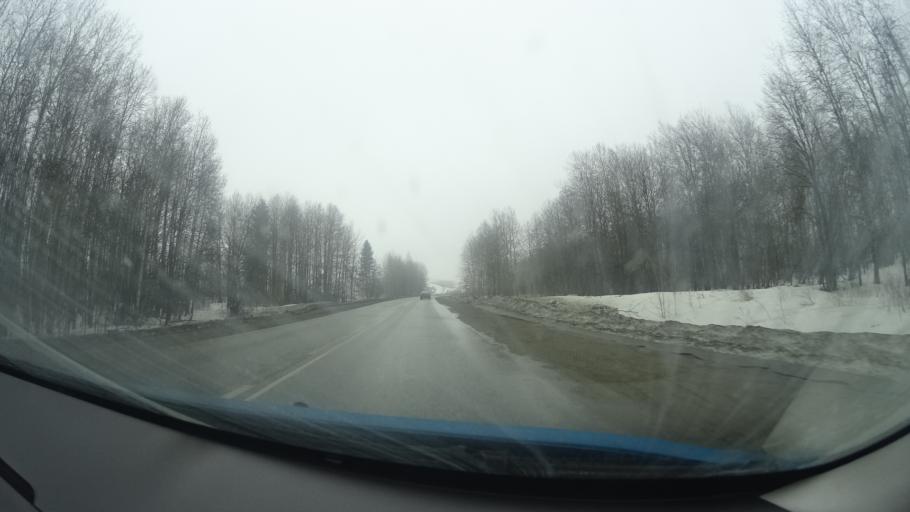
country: RU
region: Perm
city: Kuyeda
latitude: 56.4582
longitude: 55.6266
